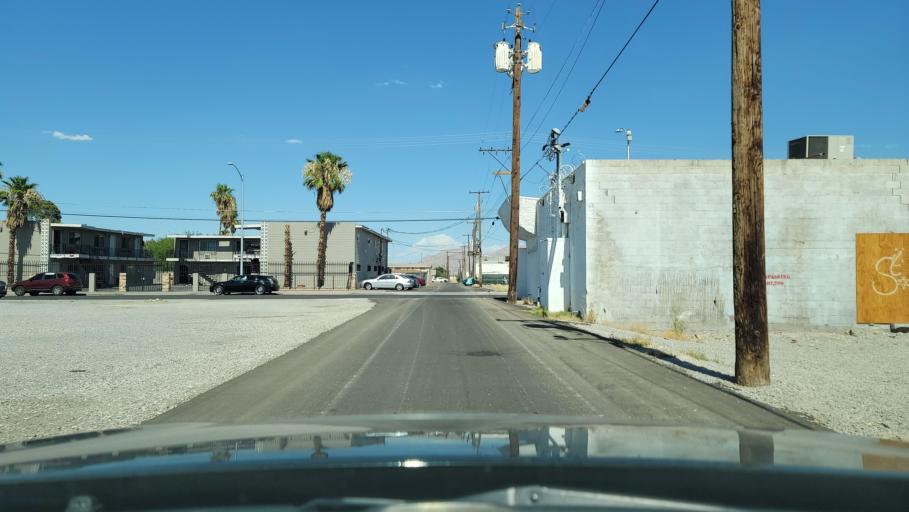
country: US
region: Nevada
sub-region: Clark County
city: Las Vegas
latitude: 36.1864
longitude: -115.1502
